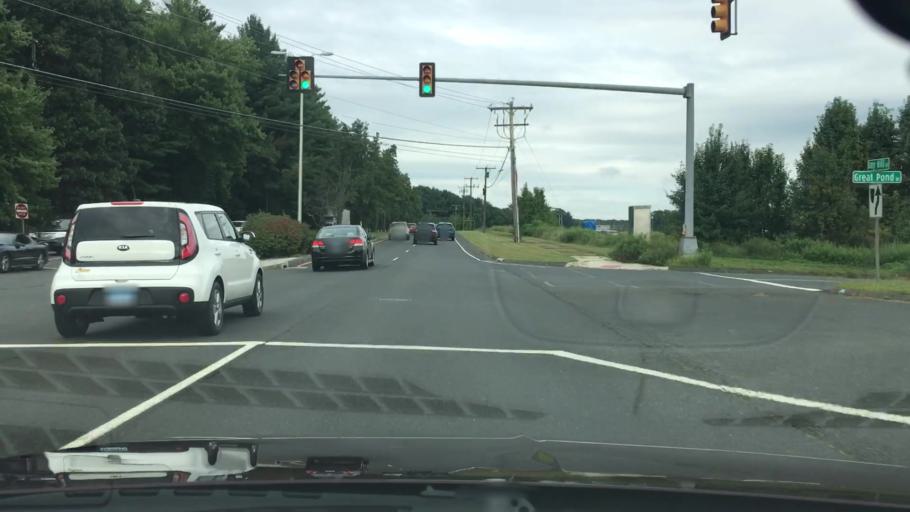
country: US
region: Connecticut
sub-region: Hartford County
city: Tariffville
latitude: 41.8779
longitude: -72.7159
